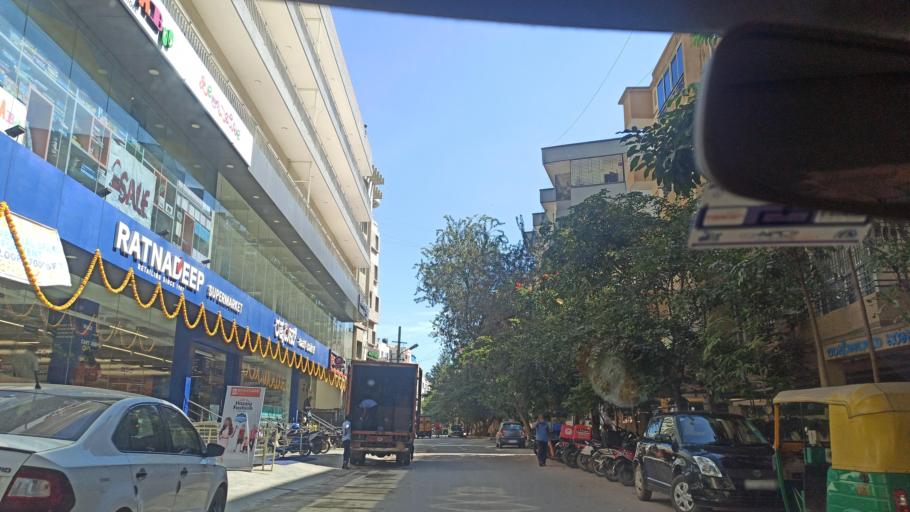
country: IN
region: Karnataka
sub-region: Bangalore Urban
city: Bangalore
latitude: 12.9272
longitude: 77.6703
